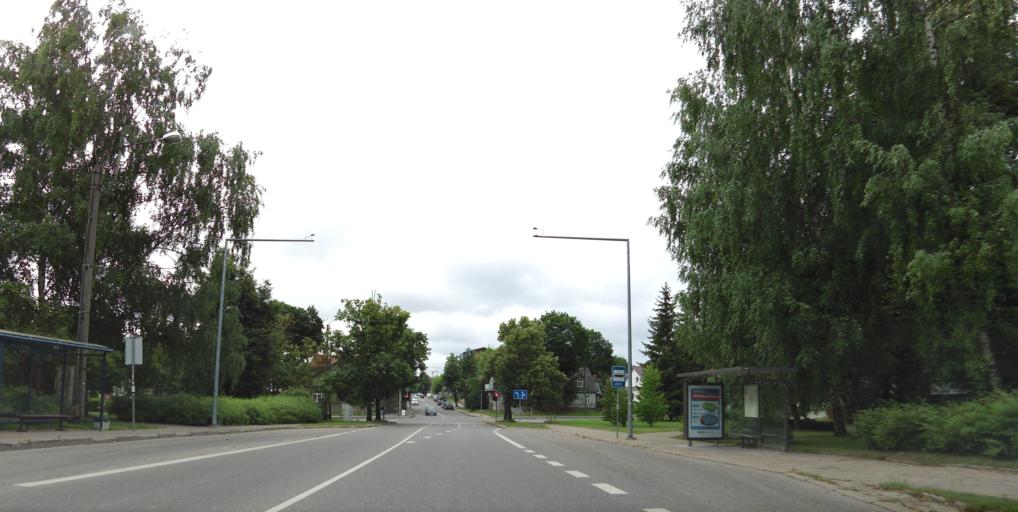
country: LT
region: Vilnius County
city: Seskine
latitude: 54.6960
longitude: 25.2559
